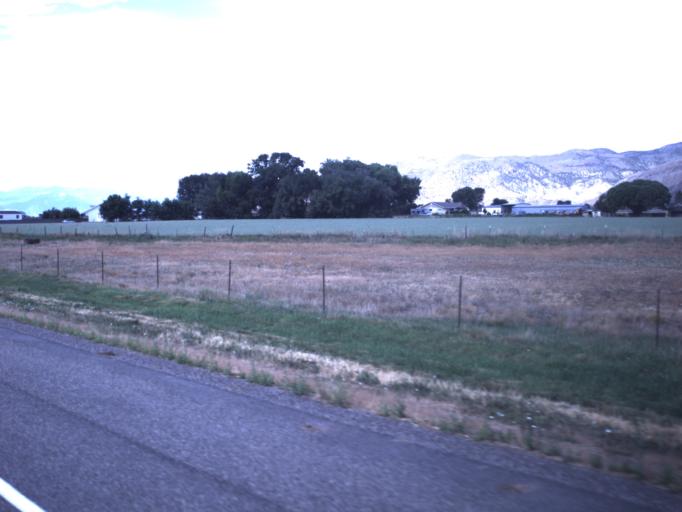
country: US
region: Utah
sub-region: Sevier County
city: Richfield
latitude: 38.7246
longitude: -112.1000
